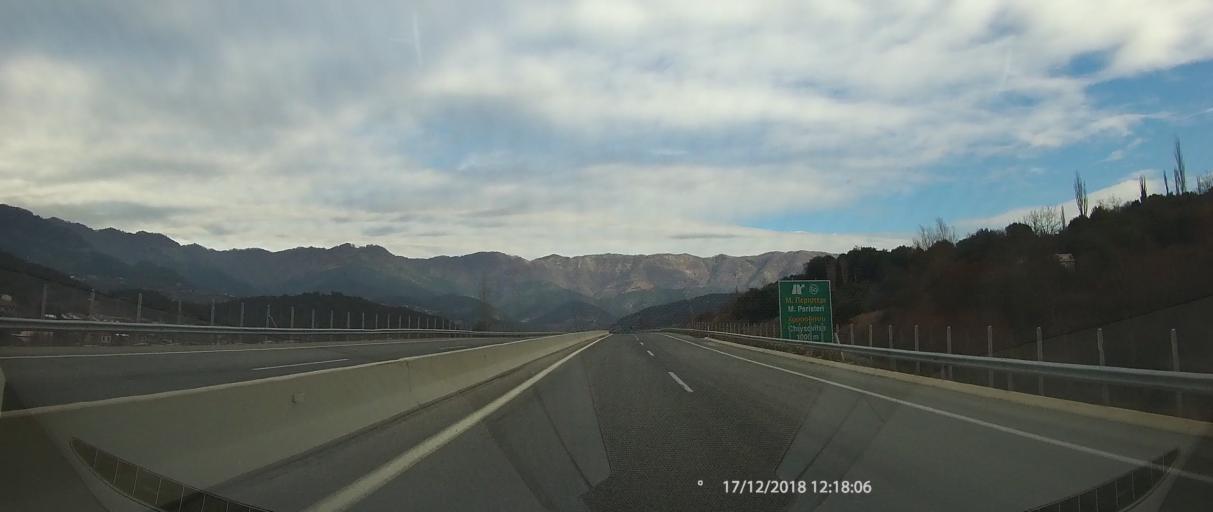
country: GR
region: Epirus
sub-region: Nomos Ioanninon
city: Metsovo
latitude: 39.7487
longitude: 21.0762
